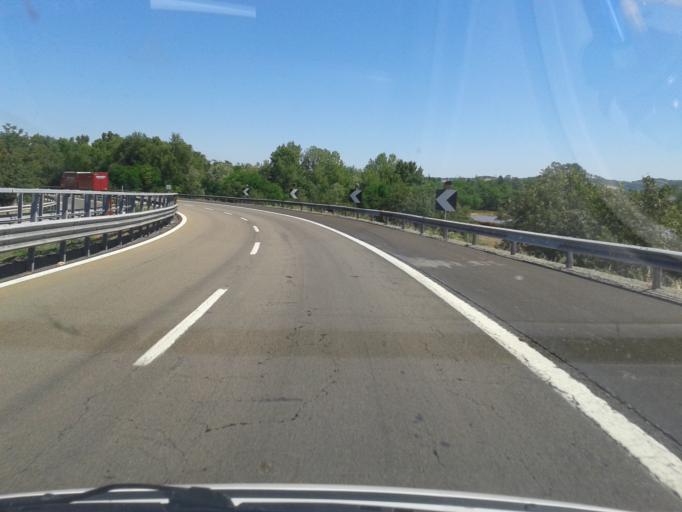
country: IT
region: Piedmont
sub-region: Provincia di Alessandria
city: Villalvernia
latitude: 44.8339
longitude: 8.8296
